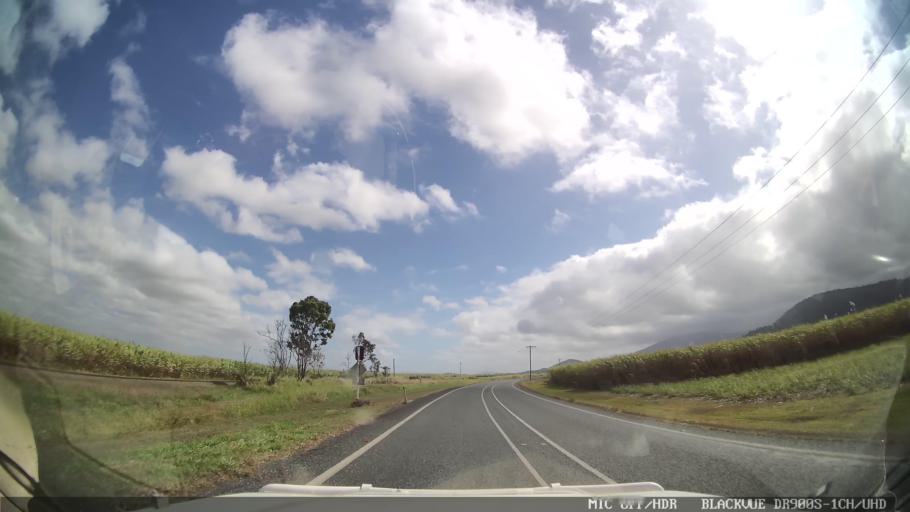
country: AU
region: Queensland
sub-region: Whitsunday
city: Proserpine
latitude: -20.3471
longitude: 148.5536
